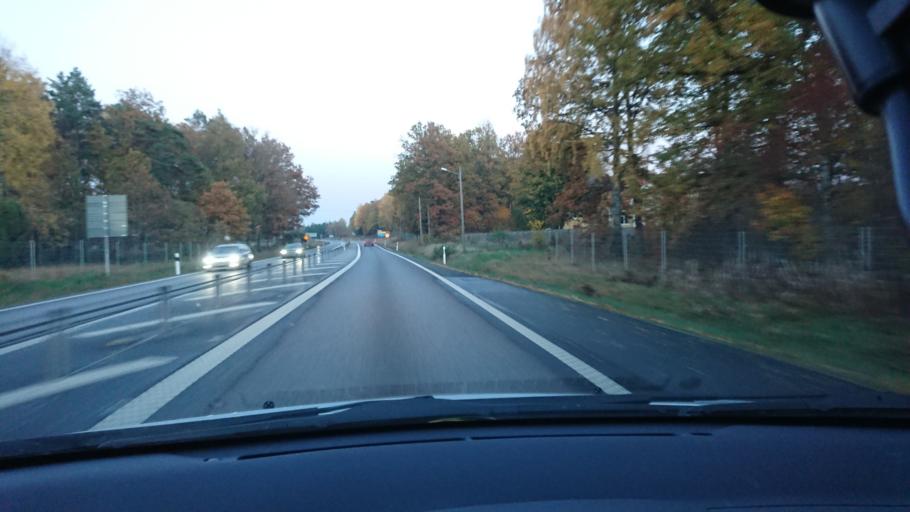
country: SE
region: Kronoberg
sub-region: Ljungby Kommun
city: Ljungby
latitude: 56.7611
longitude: 13.7789
